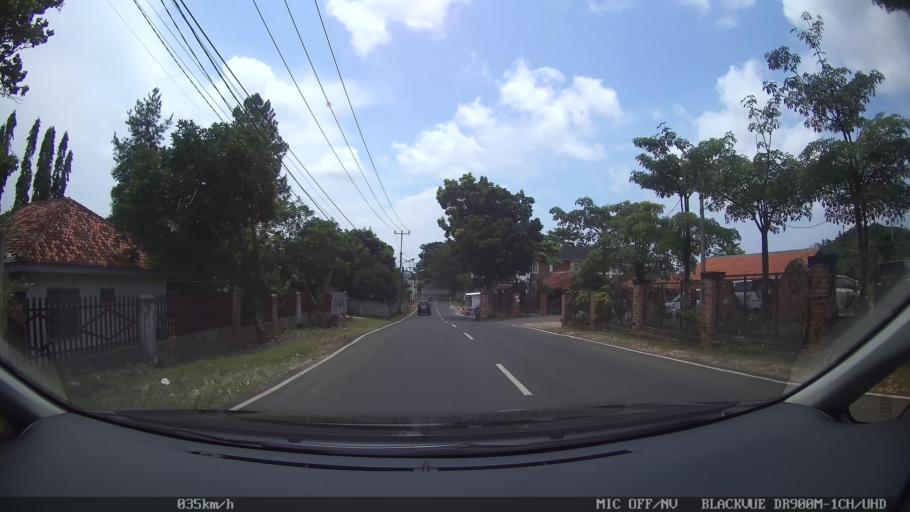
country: ID
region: Lampung
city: Bandarlampung
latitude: -5.4134
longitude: 105.2341
